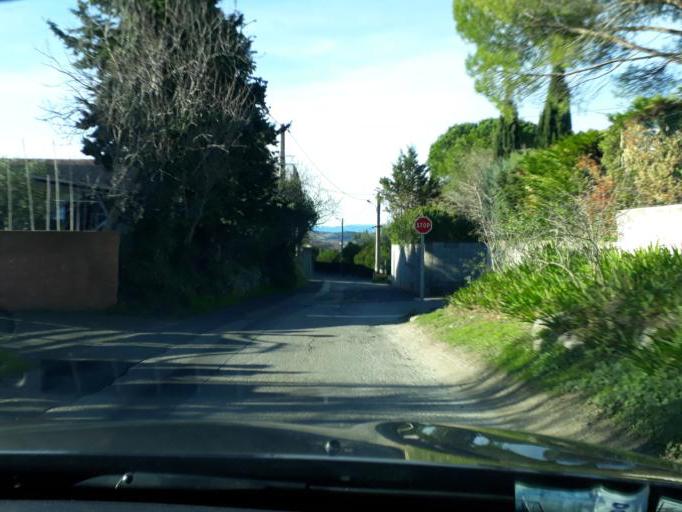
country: FR
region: Languedoc-Roussillon
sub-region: Departement de l'Herault
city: Castelnau-de-Guers
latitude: 43.4367
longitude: 3.4416
